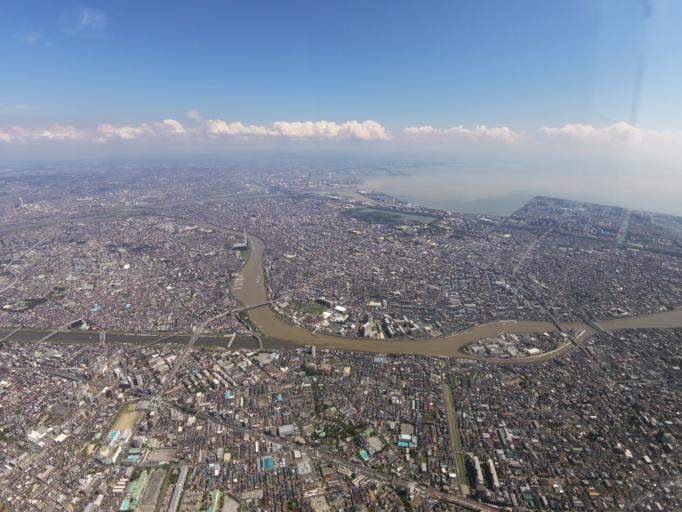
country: JP
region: Tokyo
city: Urayasu
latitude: 35.6768
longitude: 139.8697
